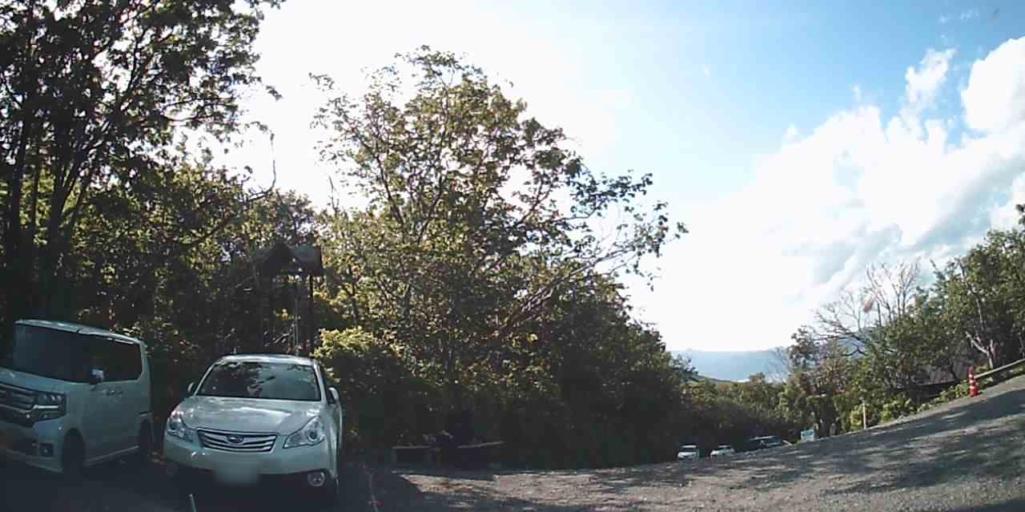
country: JP
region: Hokkaido
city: Shiraoi
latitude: 42.6990
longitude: 141.3902
